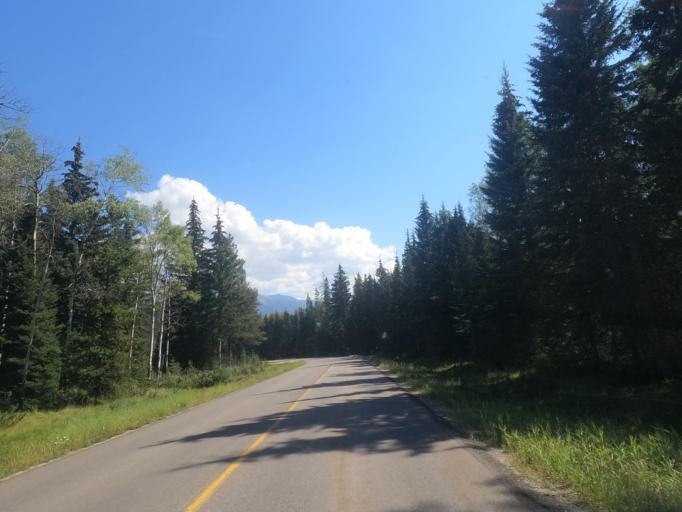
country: CA
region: Alberta
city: Jasper Park Lodge
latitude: 52.8543
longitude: -118.0898
